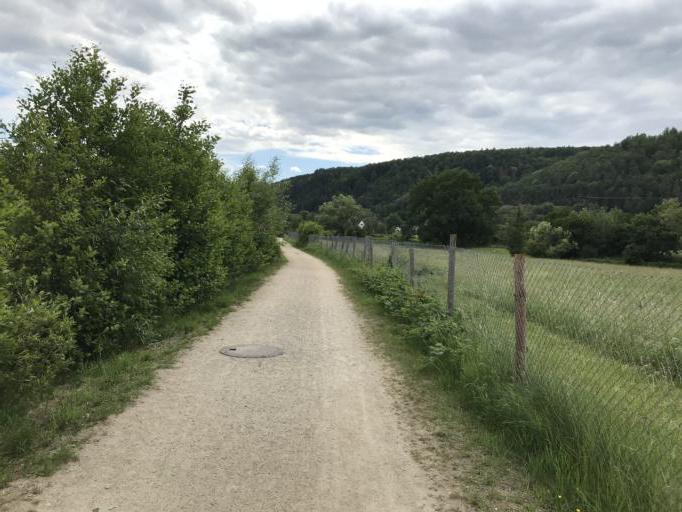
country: DE
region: Baden-Wuerttemberg
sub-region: Freiburg Region
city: Hausen
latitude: 47.6694
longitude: 7.8358
